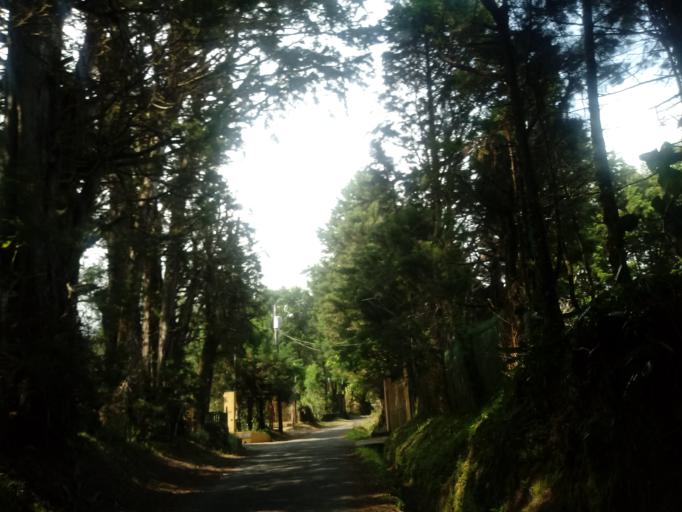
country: CR
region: Heredia
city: Angeles
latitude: 10.0401
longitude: -84.0415
